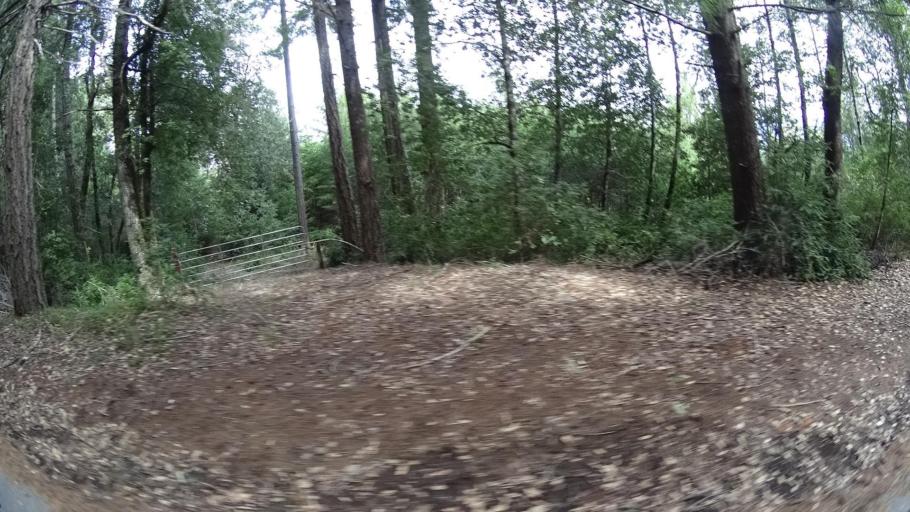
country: US
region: California
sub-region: Humboldt County
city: Redway
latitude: 40.0634
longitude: -123.8298
